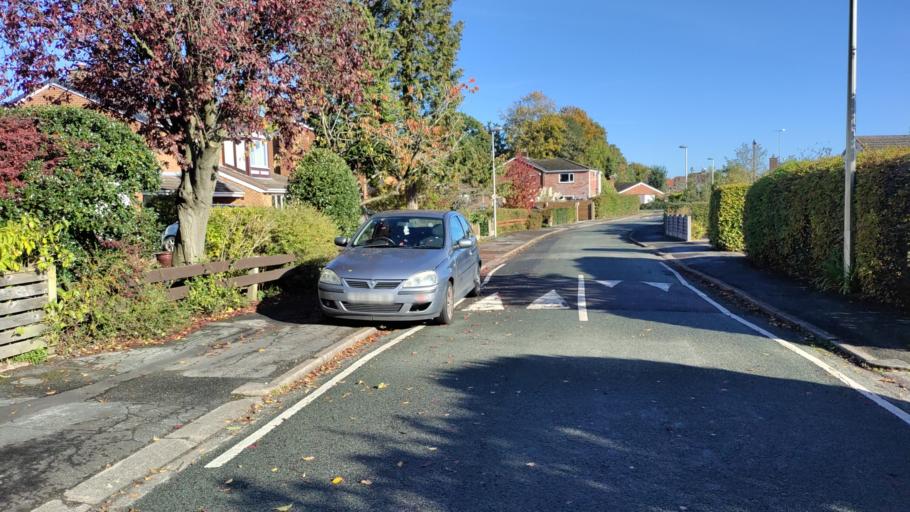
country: GB
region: England
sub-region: Cheshire West and Chester
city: Hartford
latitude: 53.2428
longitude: -2.5459
